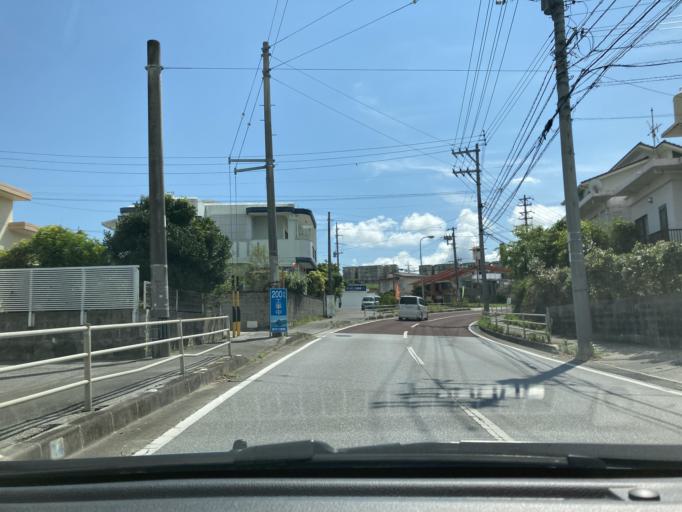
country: JP
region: Okinawa
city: Tomigusuku
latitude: 26.1811
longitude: 127.7418
